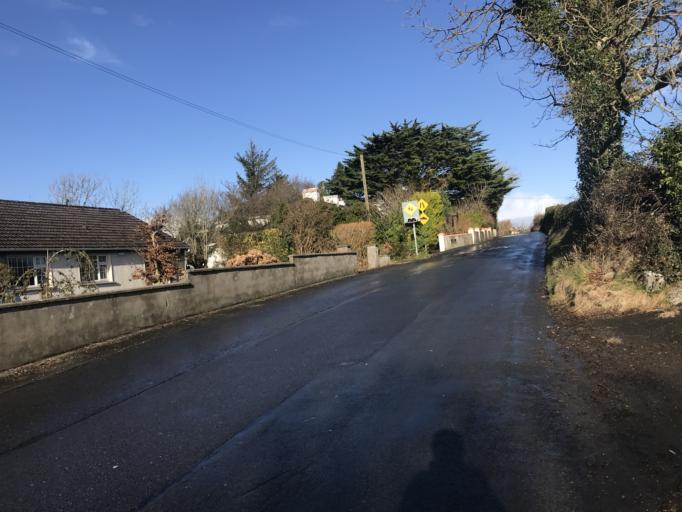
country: IE
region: Connaught
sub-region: County Galway
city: Gaillimh
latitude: 53.3000
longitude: -9.0184
